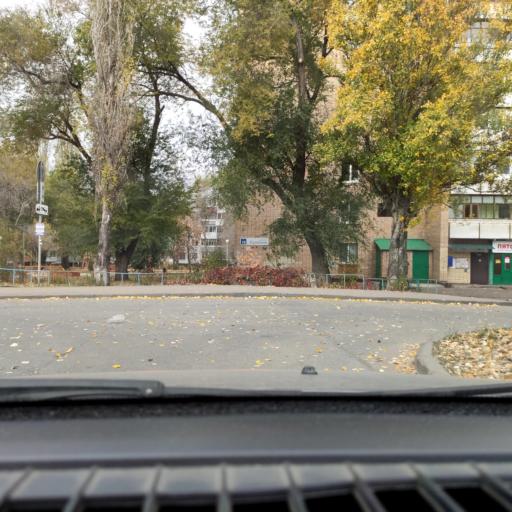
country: RU
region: Samara
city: Tol'yatti
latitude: 53.5344
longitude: 49.2674
